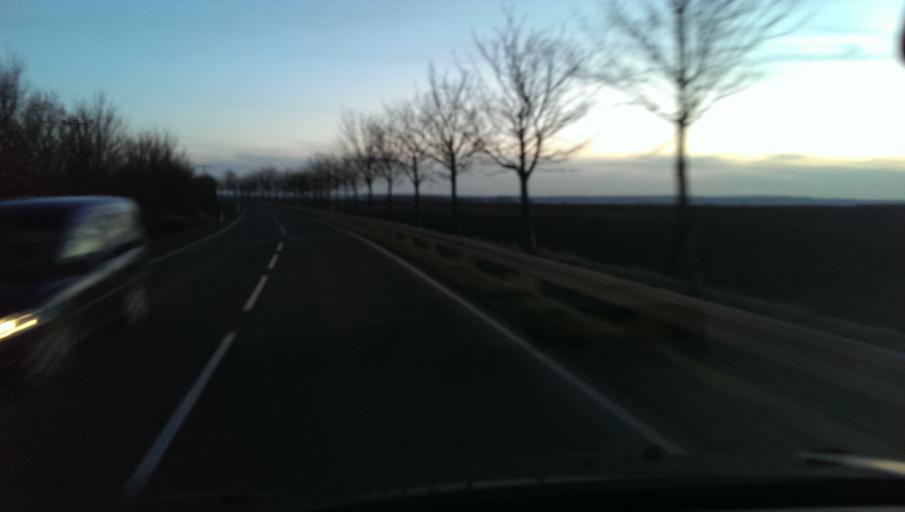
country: DE
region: Saxony-Anhalt
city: Ausleben
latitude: 52.0571
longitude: 11.0850
